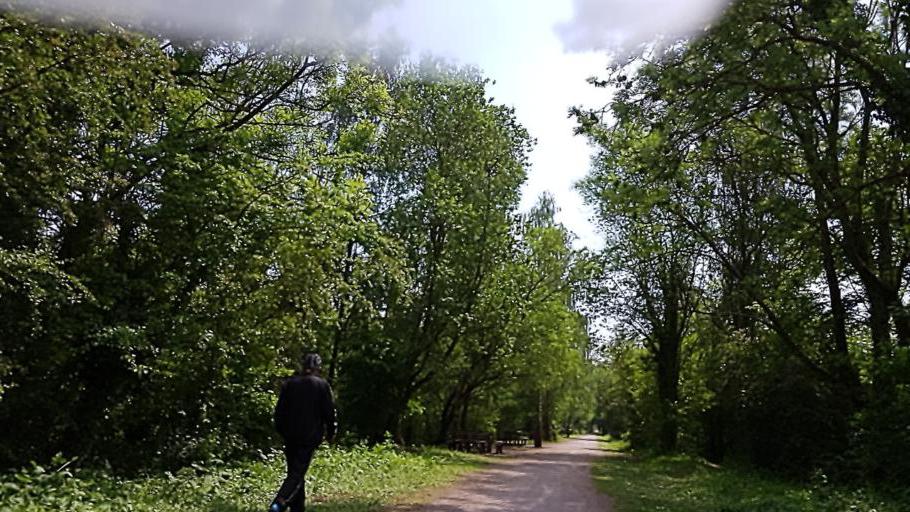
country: FR
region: Nord-Pas-de-Calais
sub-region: Departement du Nord
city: Conde-sur-l'Escaut
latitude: 50.4500
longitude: 3.5829
